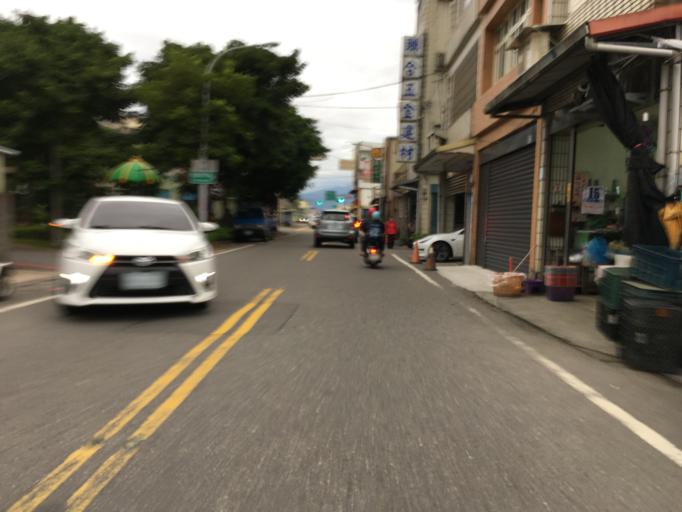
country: TW
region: Taiwan
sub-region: Yilan
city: Yilan
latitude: 24.6844
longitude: 121.7677
